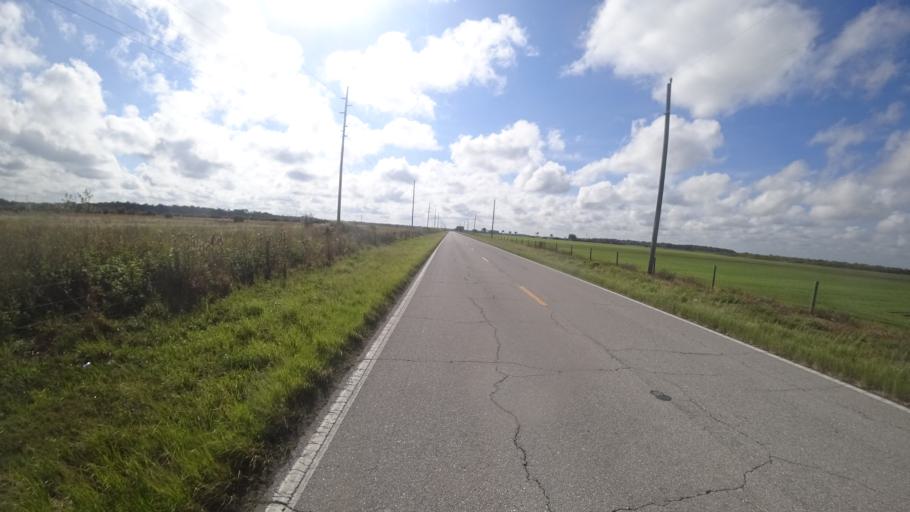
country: US
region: Florida
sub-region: Hardee County
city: Wauchula
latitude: 27.5316
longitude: -82.0774
